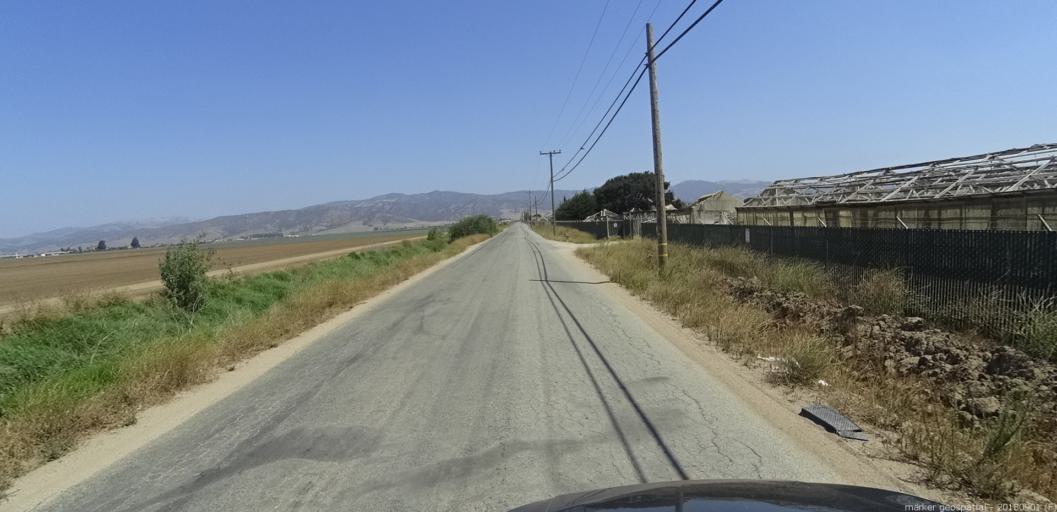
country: US
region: California
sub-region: Monterey County
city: Chualar
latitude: 36.6087
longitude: -121.5526
